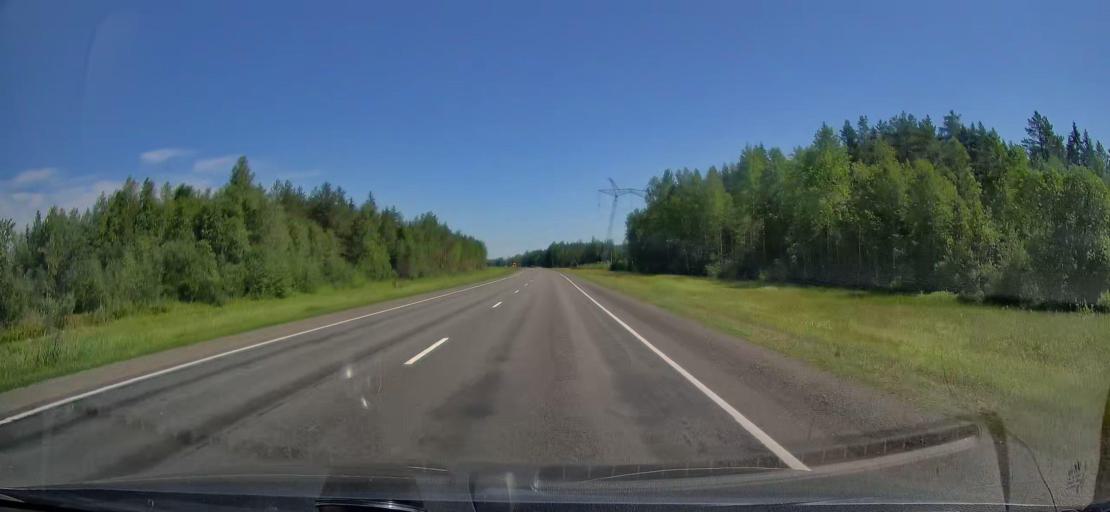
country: RU
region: Tverskaya
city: Ves'yegonsk
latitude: 58.9223
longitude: 37.2239
